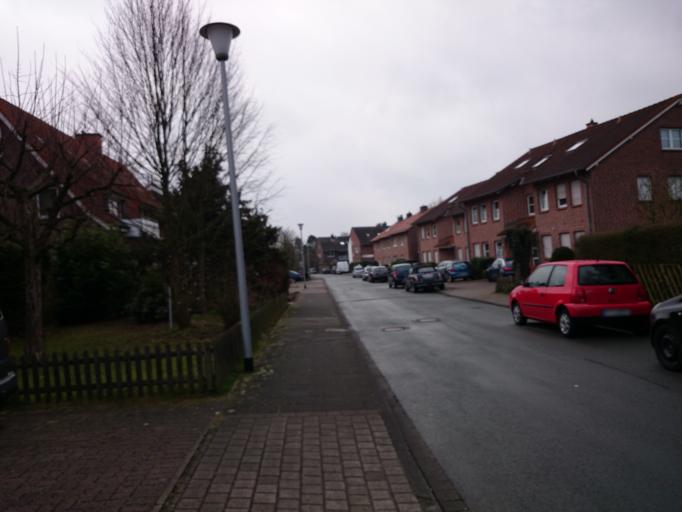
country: DE
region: North Rhine-Westphalia
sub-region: Regierungsbezirk Munster
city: Muenster
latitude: 51.9292
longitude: 7.5831
